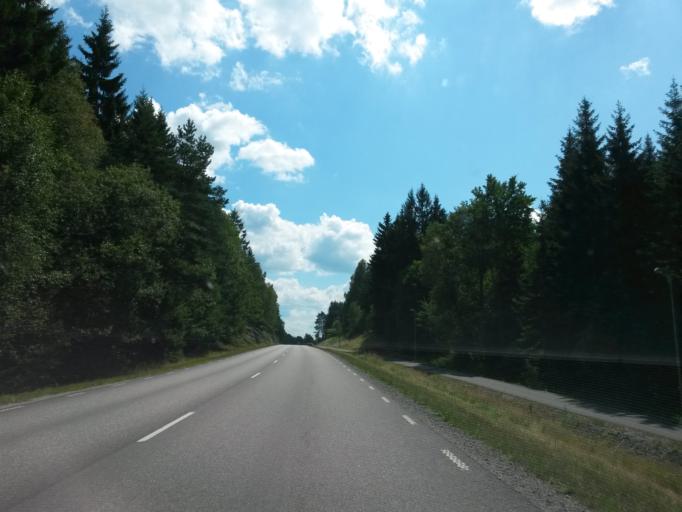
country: SE
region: Vaestra Goetaland
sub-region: Lerums Kommun
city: Grabo
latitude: 57.8245
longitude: 12.2934
